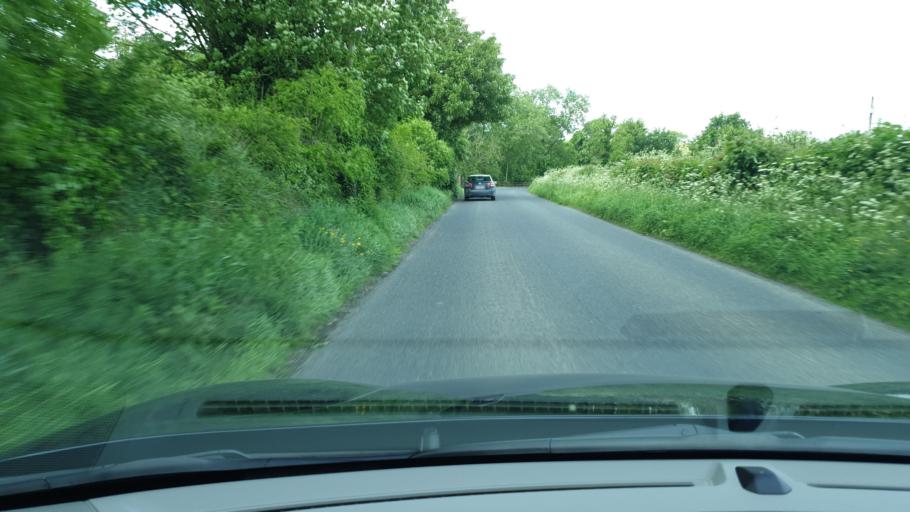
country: IE
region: Leinster
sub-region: Lu
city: Ardee
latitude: 53.8127
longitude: -6.6411
